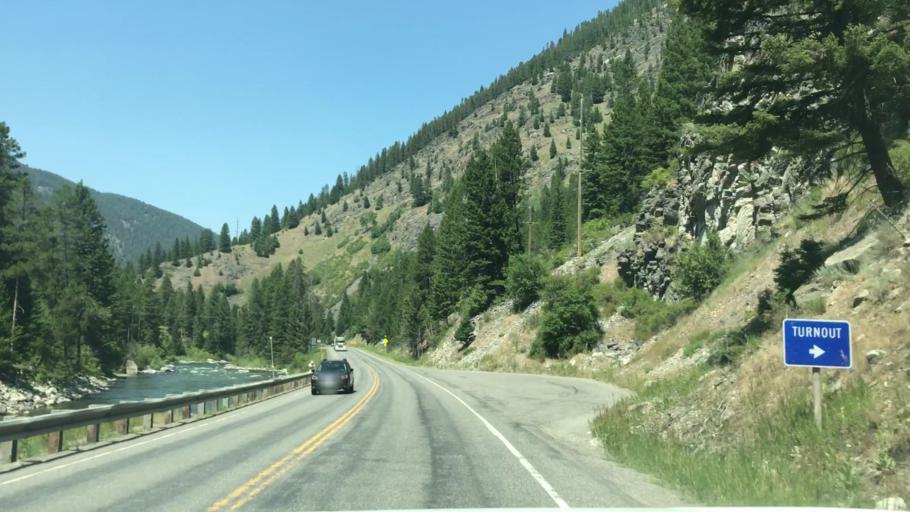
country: US
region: Montana
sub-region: Gallatin County
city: Big Sky
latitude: 45.4036
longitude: -111.2186
